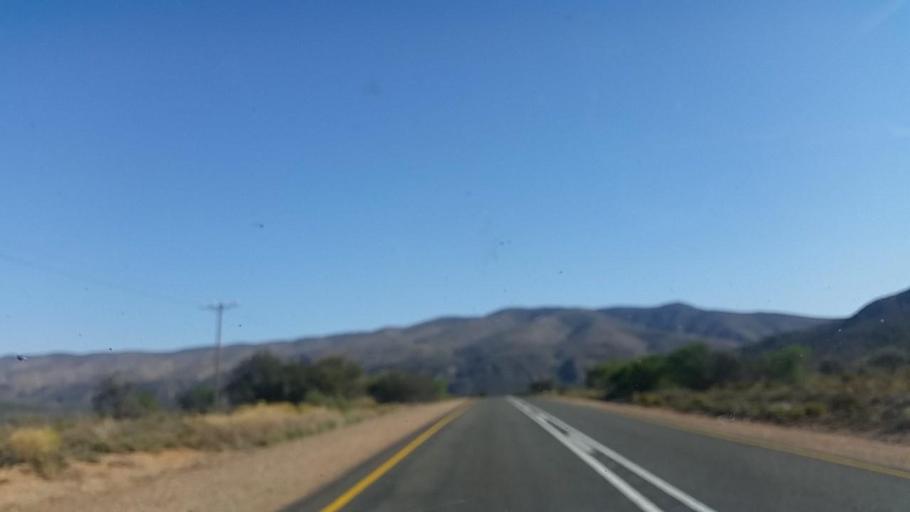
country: ZA
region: Eastern Cape
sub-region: Cacadu District Municipality
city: Willowmore
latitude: -33.4337
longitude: 23.3074
